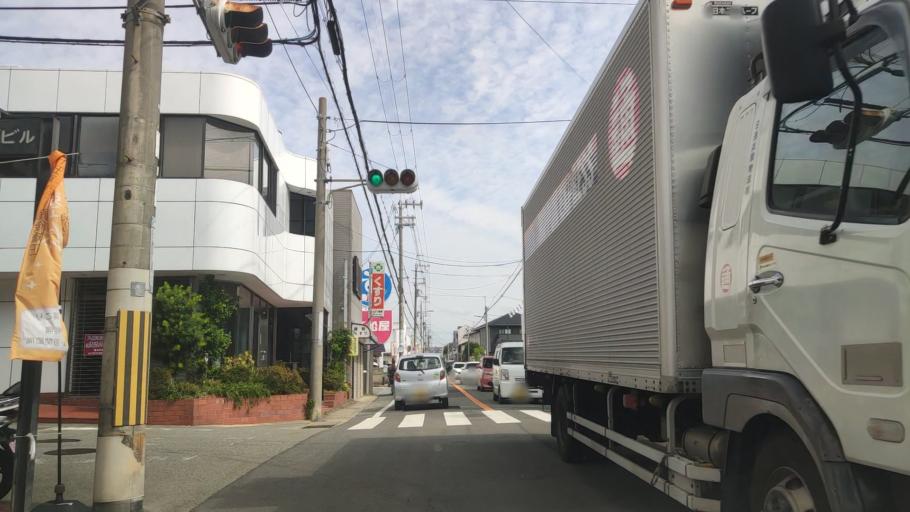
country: JP
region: Osaka
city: Mino
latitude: 34.8124
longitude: 135.4683
